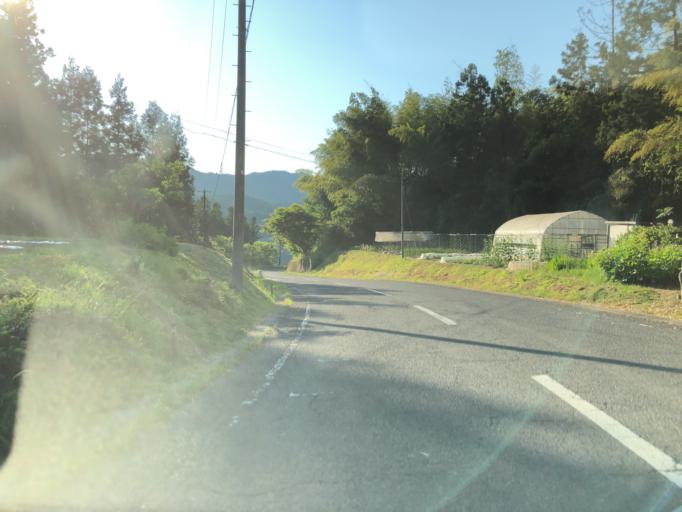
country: JP
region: Ibaraki
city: Daigo
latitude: 36.9304
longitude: 140.4492
